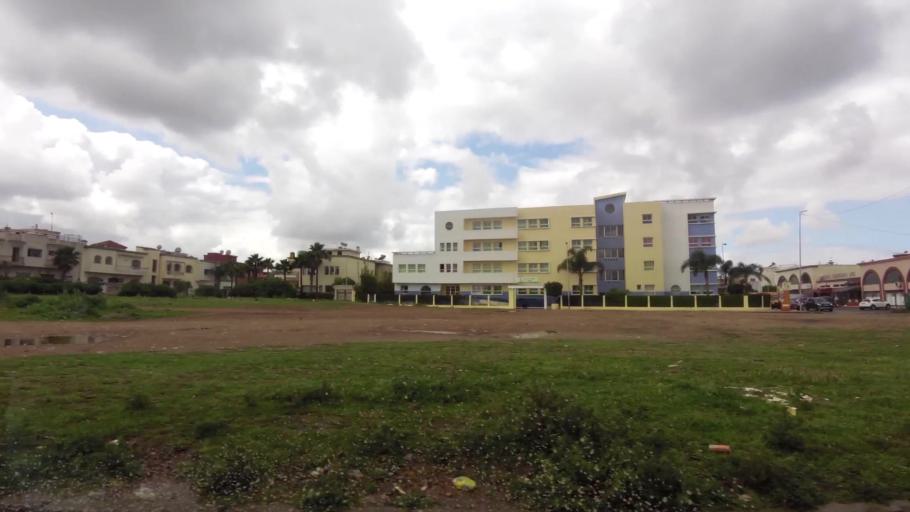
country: MA
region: Grand Casablanca
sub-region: Nouaceur
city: Bouskoura
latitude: 33.5187
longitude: -7.6436
